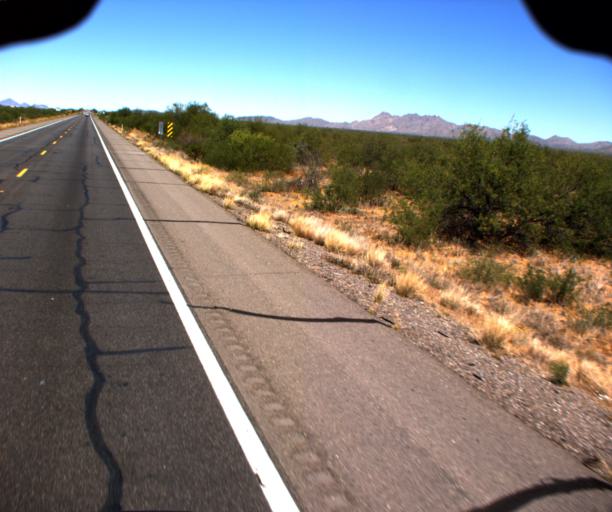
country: US
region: Arizona
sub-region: Yavapai County
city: Congress
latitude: 34.1155
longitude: -112.9391
